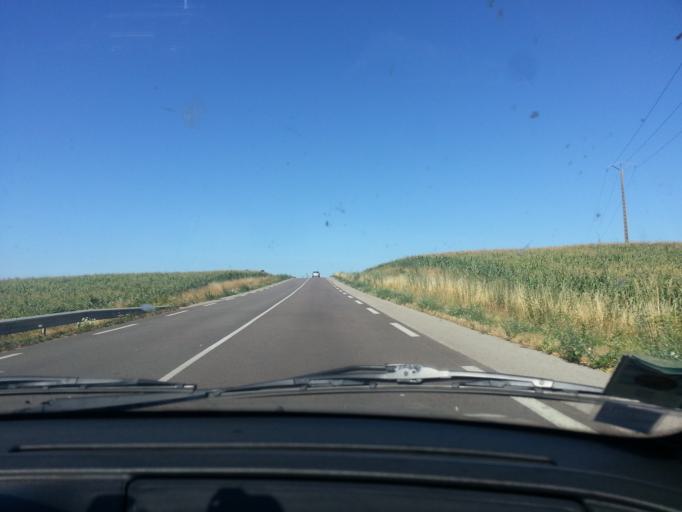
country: FR
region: Bourgogne
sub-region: Departement de Saone-et-Loire
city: Sassenay
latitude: 46.8047
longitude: 4.9426
